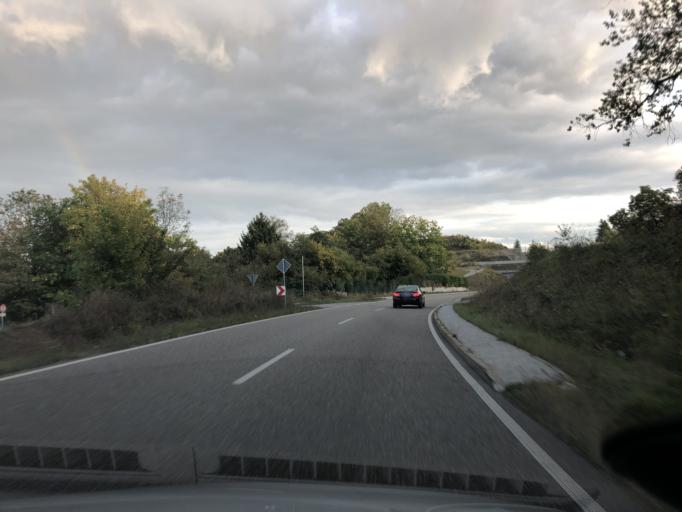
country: DE
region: Baden-Wuerttemberg
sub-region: Karlsruhe Region
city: Wimsheim
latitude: 48.8422
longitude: 8.8301
